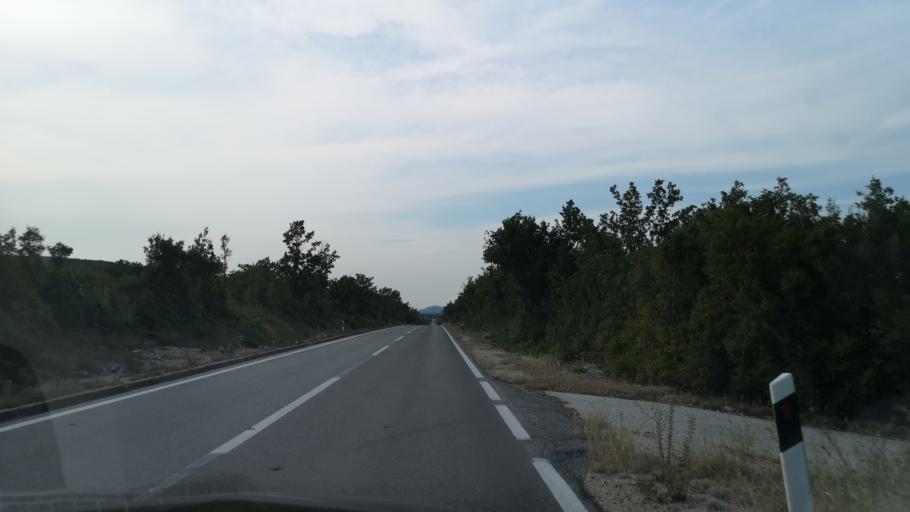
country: HR
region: Sibensko-Kniniska
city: Zaton
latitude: 43.8430
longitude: 15.7738
